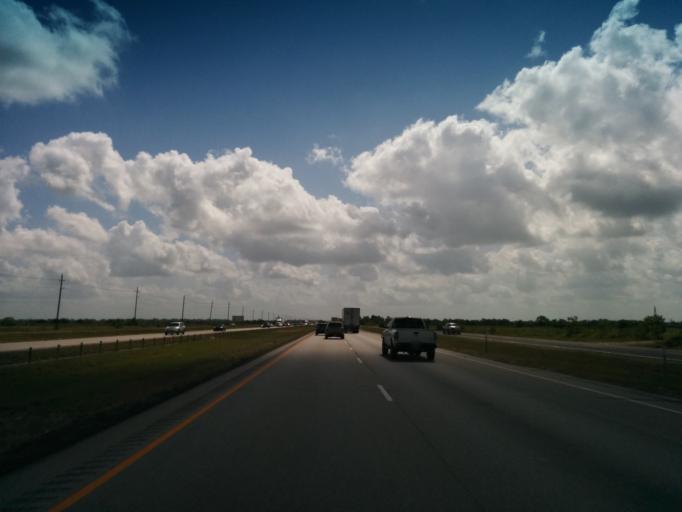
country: US
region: Texas
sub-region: Austin County
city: Sealy
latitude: 29.7597
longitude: -96.2138
